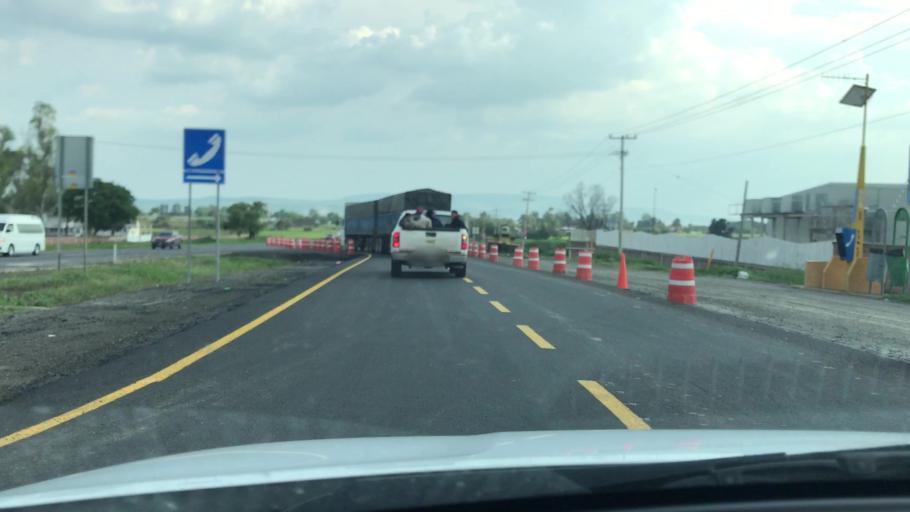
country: MX
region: Guanajuato
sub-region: Irapuato
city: San Ignacio de Rivera (Ojo de Agua)
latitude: 20.5328
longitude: -101.4598
